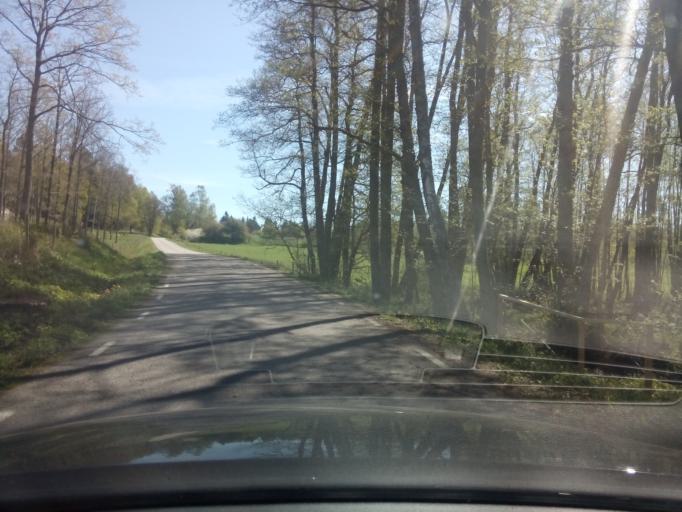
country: SE
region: Soedermanland
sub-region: Trosa Kommun
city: Trosa
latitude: 58.7974
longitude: 17.3739
